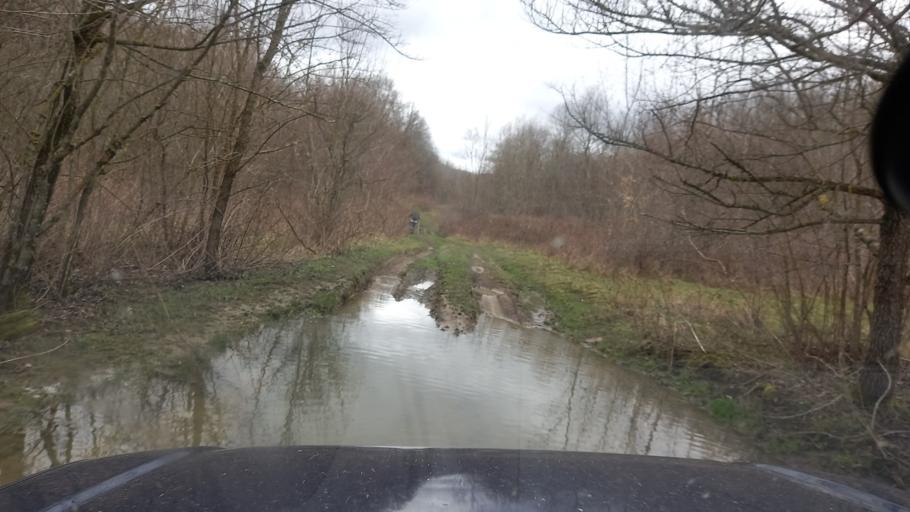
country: RU
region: Krasnodarskiy
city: Pshada
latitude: 44.4864
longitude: 38.3983
